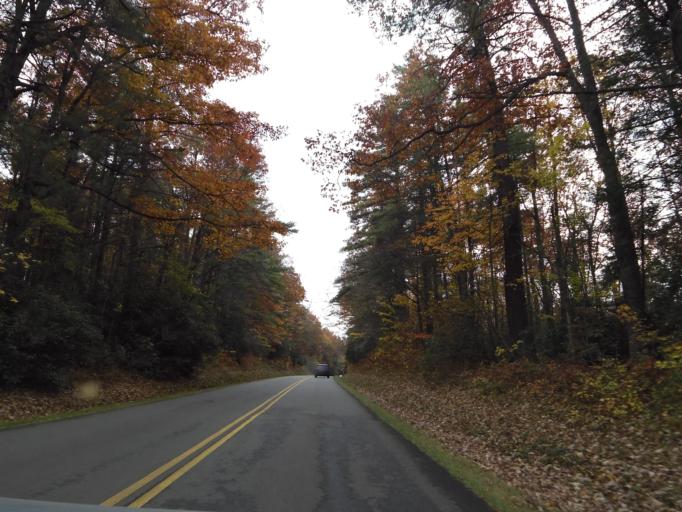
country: US
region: North Carolina
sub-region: Ashe County
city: Jefferson
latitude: 36.3514
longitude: -81.3727
